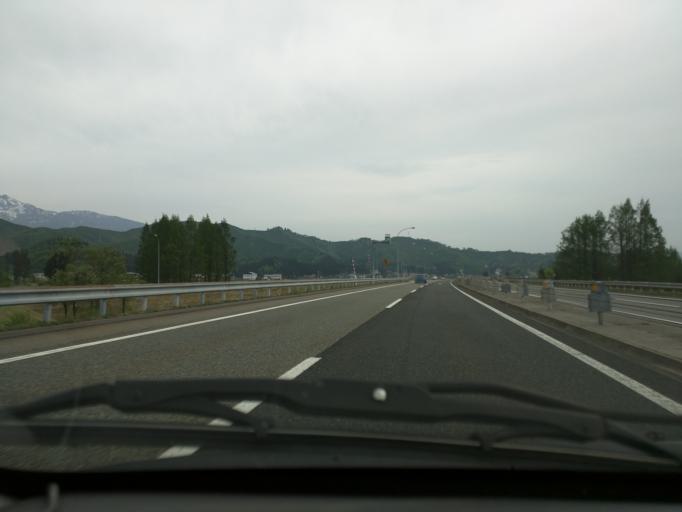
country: JP
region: Niigata
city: Muikamachi
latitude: 37.2159
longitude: 138.9749
